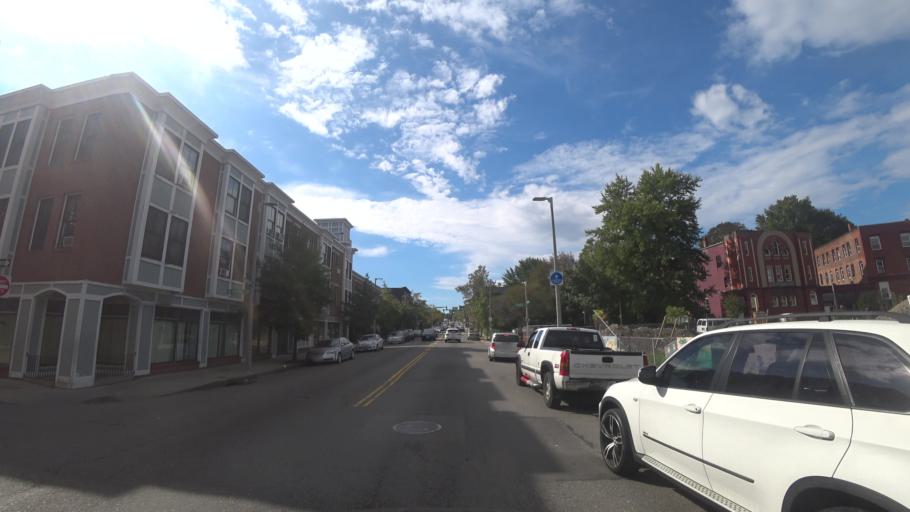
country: US
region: Massachusetts
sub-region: Suffolk County
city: South Boston
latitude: 42.3129
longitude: -71.0801
